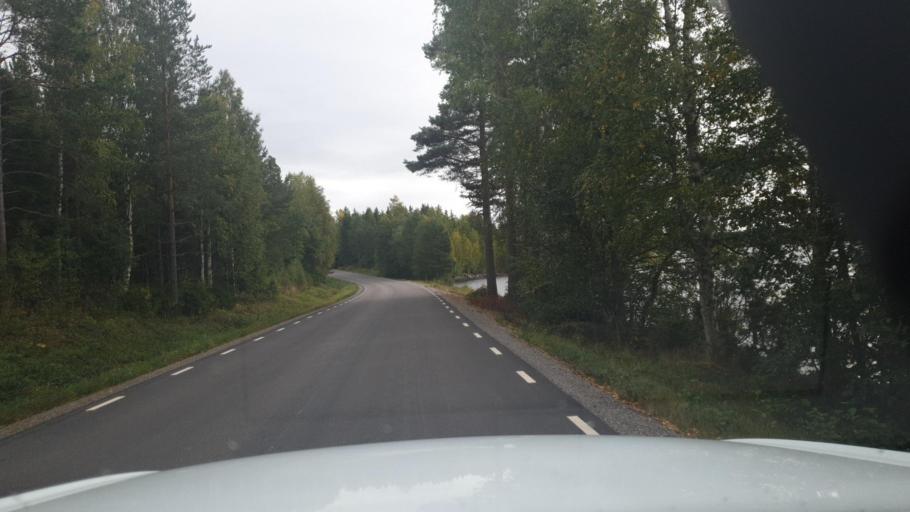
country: SE
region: Vaermland
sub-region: Torsby Kommun
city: Torsby
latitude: 60.0039
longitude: 12.7207
